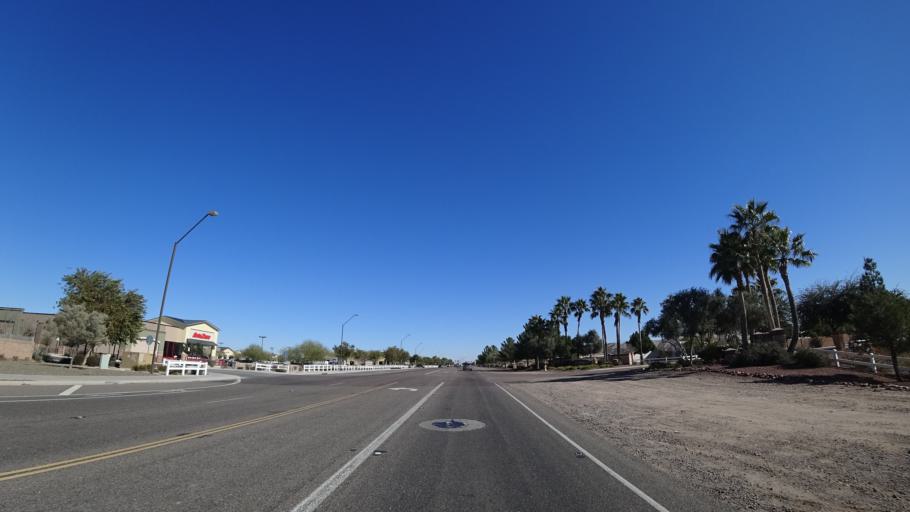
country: US
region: Arizona
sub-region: Maricopa County
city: Goodyear
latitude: 33.4356
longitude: -112.4141
